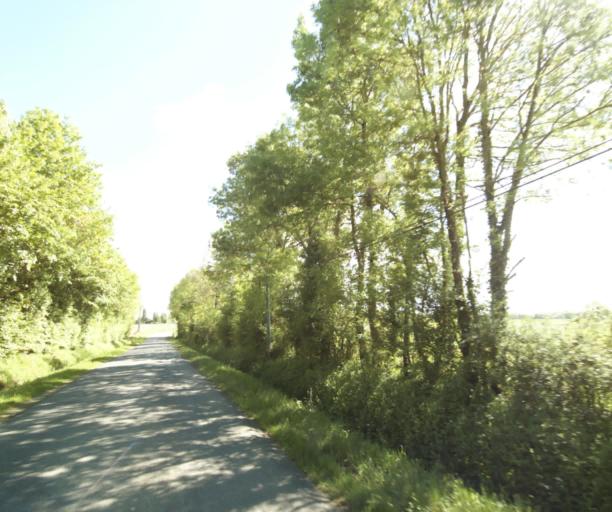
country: FR
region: Poitou-Charentes
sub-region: Departement de la Charente-Maritime
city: Saint-Georges-des-Coteaux
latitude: 45.7857
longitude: -0.6963
